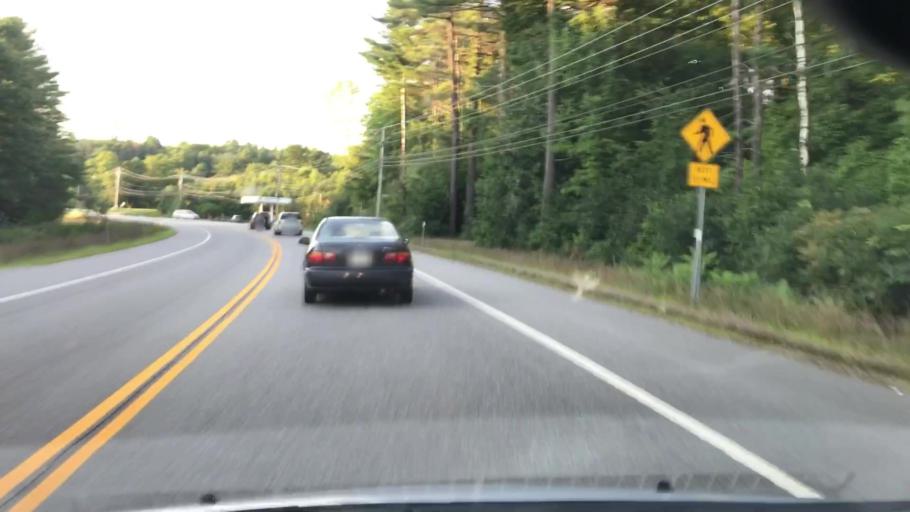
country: US
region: New Hampshire
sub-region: Grafton County
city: Rumney
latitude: 43.8645
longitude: -71.9100
